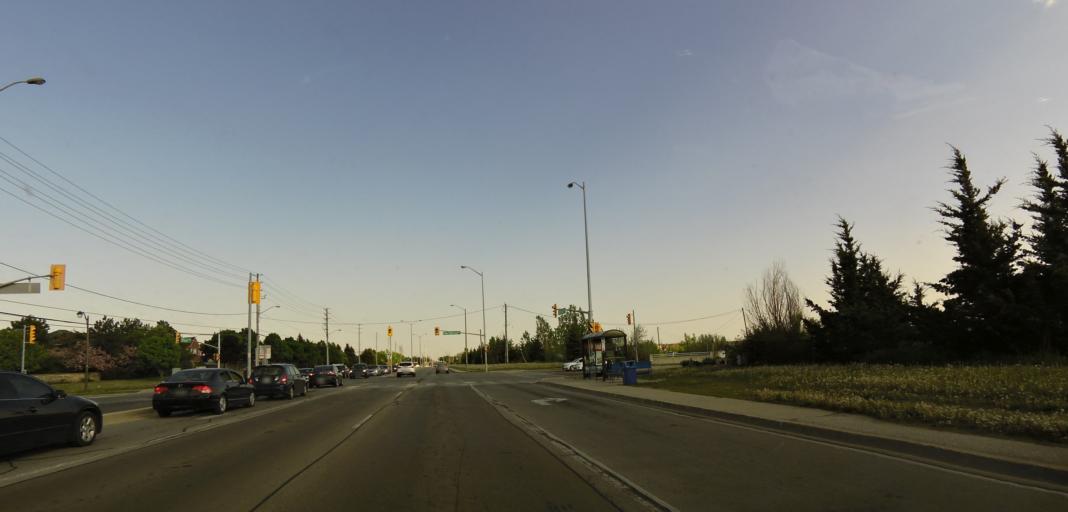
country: CA
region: Ontario
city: Brampton
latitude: 43.7390
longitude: -79.7607
